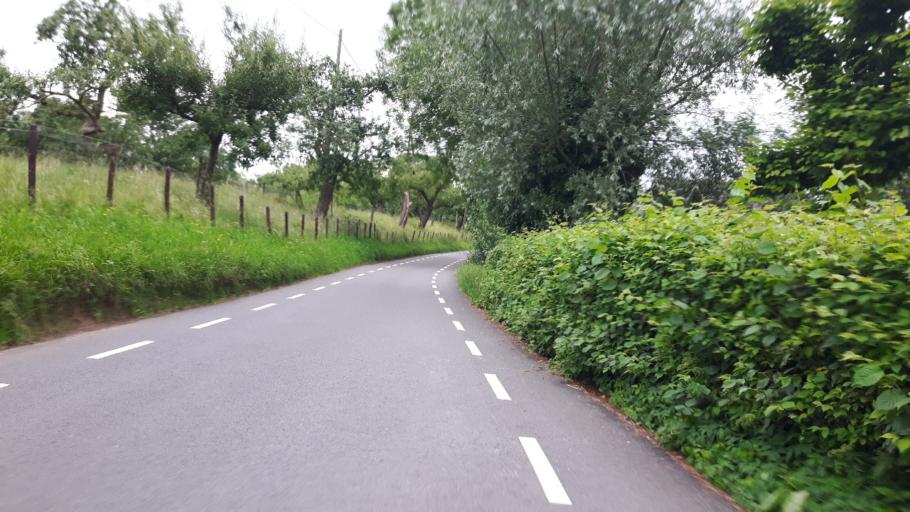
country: NL
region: Utrecht
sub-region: Gemeente Oudewater
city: Oudewater
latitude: 52.0173
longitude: 4.8342
